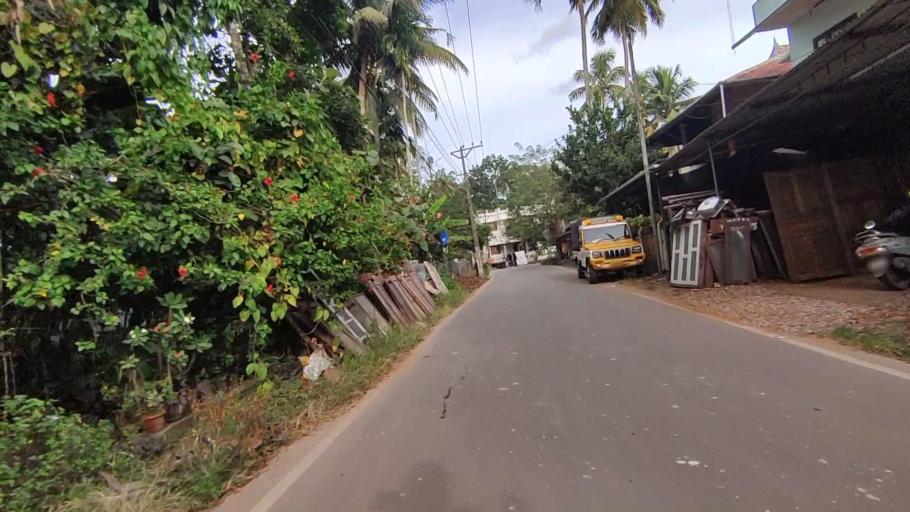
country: IN
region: Kerala
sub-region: Kottayam
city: Kottayam
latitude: 9.5931
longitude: 76.4952
